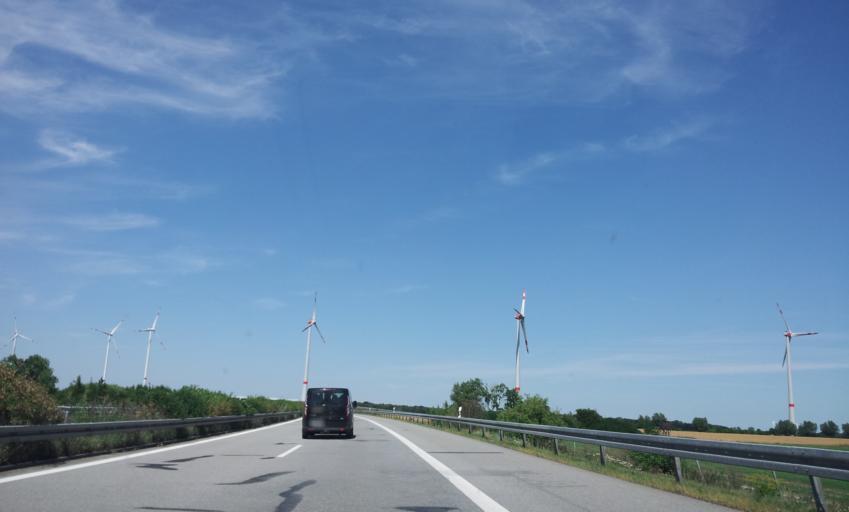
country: DE
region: Mecklenburg-Vorpommern
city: Jarmen
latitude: 53.8773
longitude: 13.3477
